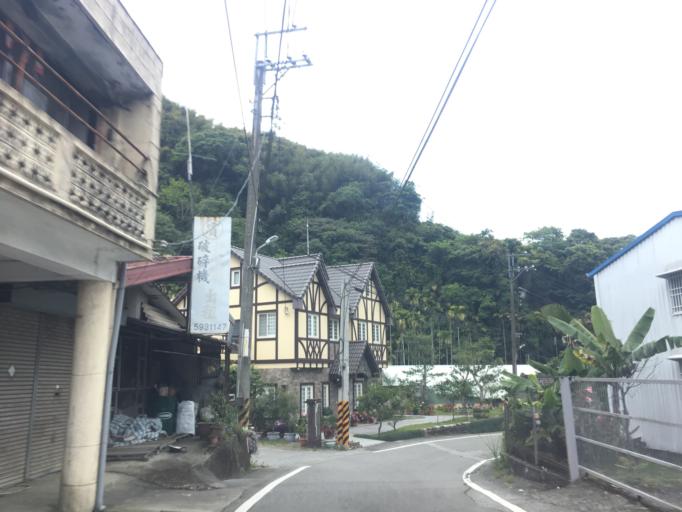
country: TW
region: Taiwan
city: Fengyuan
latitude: 24.1589
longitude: 120.8265
